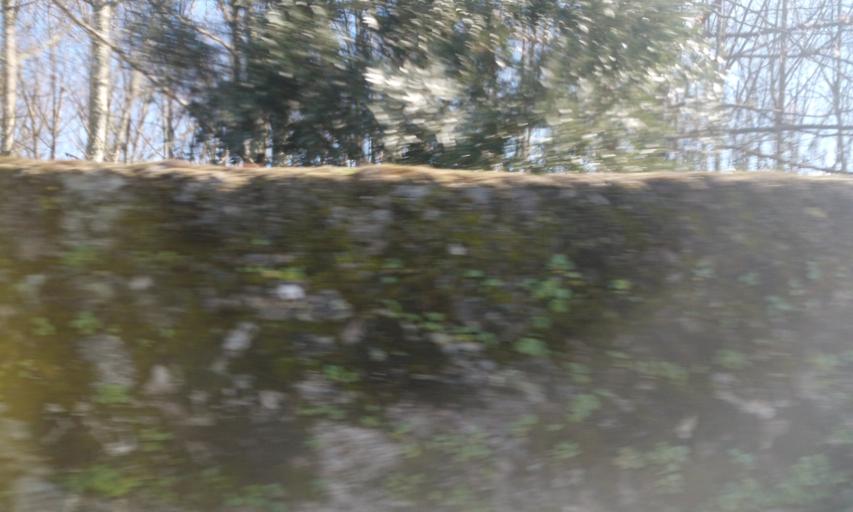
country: PT
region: Guarda
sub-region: Manteigas
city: Manteigas
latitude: 40.5060
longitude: -7.6097
